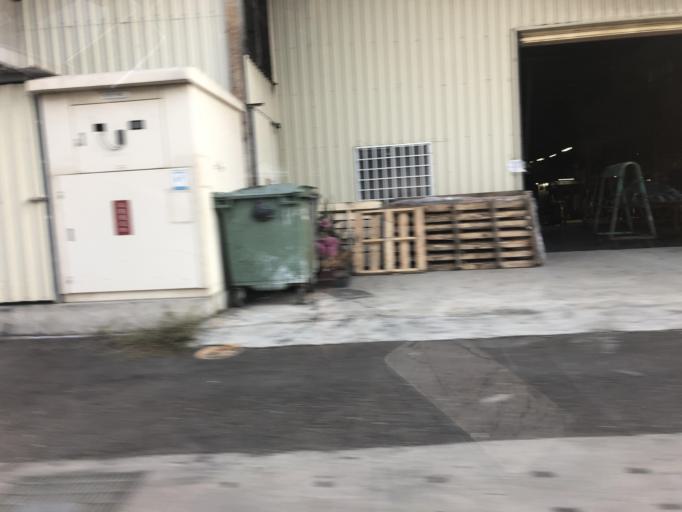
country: TW
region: Taiwan
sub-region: Tainan
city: Tainan
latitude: 23.0435
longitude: 120.2472
